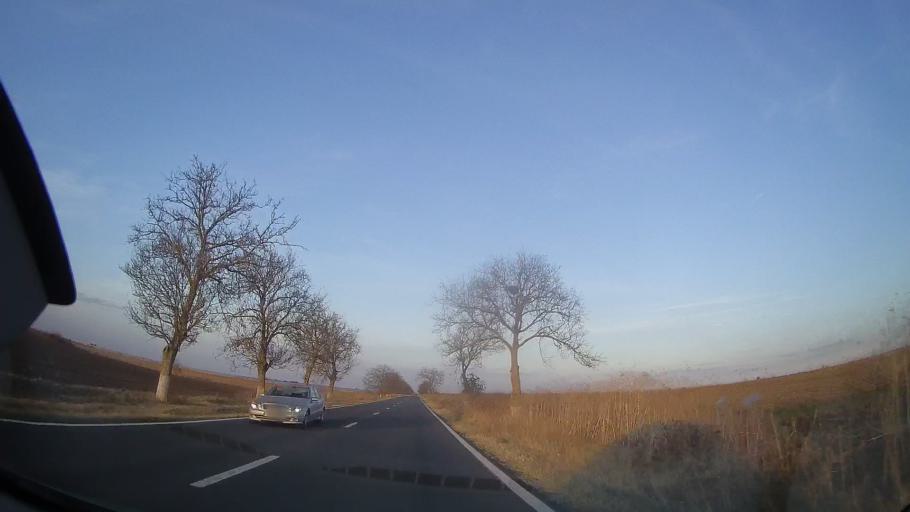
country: RO
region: Constanta
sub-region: Comuna Topraisar
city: Topraisar
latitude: 43.9932
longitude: 28.4272
